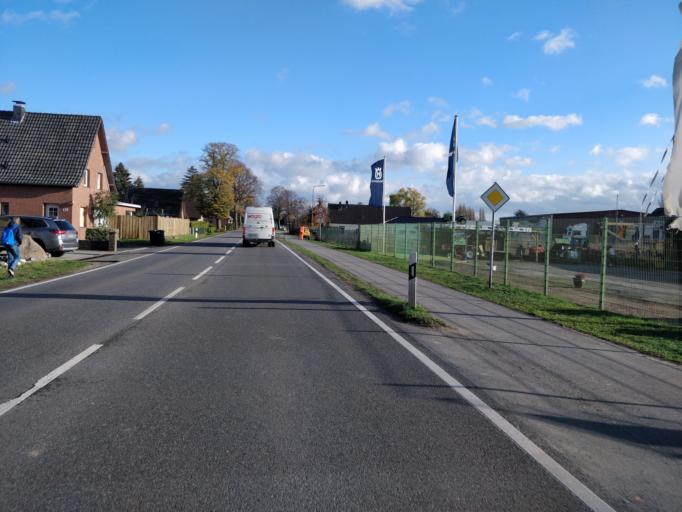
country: NL
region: Gelderland
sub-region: Oude IJsselstreek
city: Gendringen
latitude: 51.8257
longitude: 6.3218
